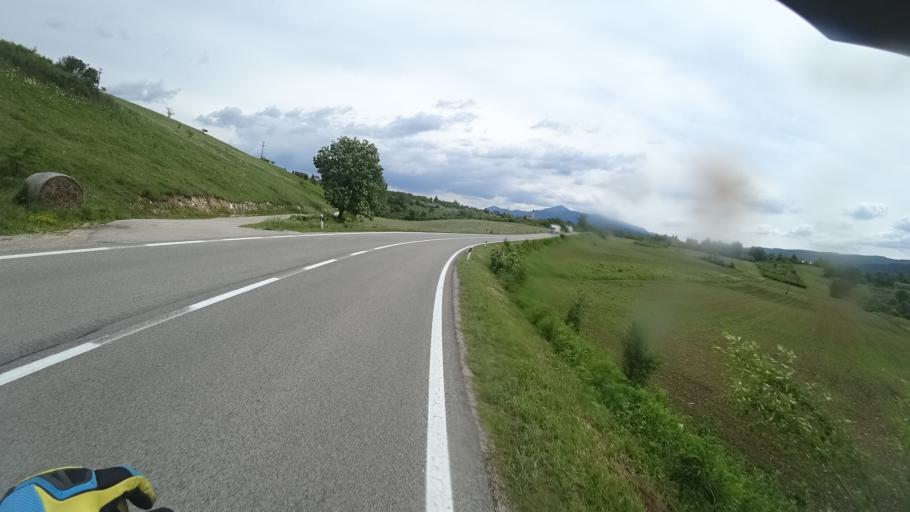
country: BA
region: Federation of Bosnia and Herzegovina
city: Izacic
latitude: 44.9139
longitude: 15.7186
